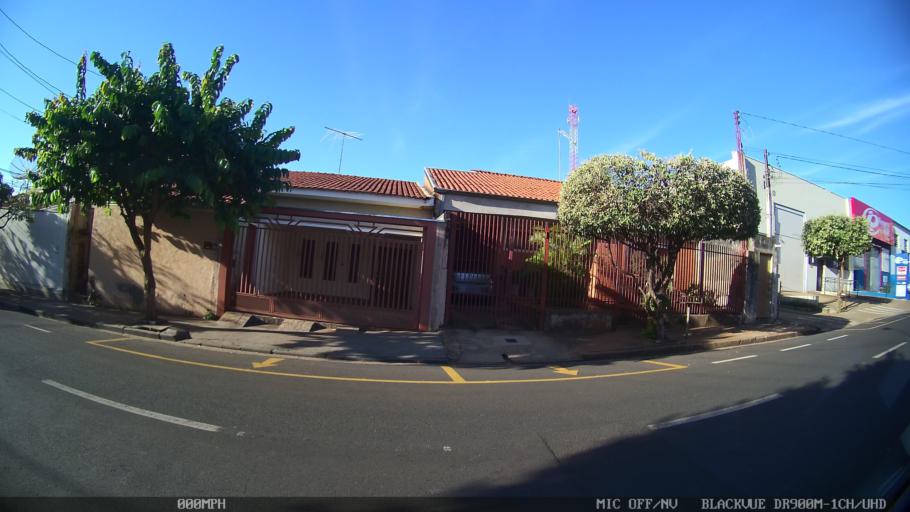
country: BR
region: Sao Paulo
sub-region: Sao Jose Do Rio Preto
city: Sao Jose do Rio Preto
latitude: -20.8247
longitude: -49.3804
